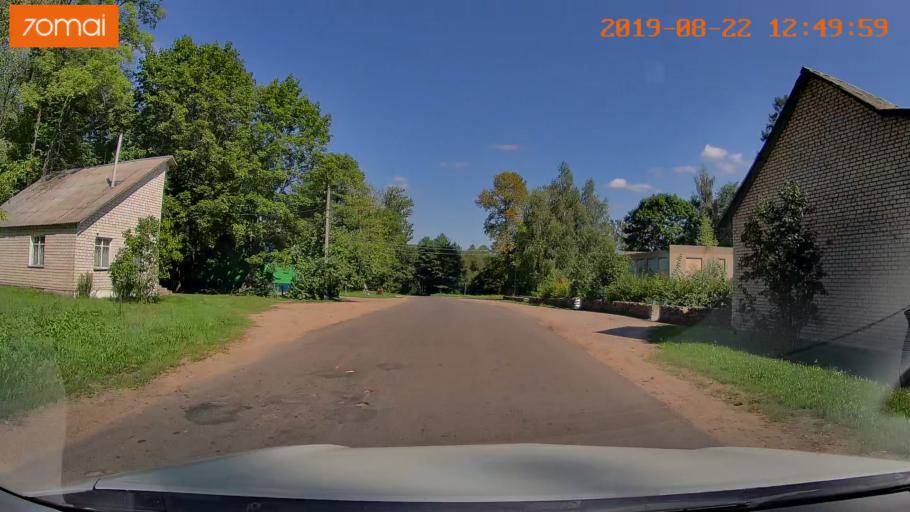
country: BY
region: Minsk
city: Prawdzinski
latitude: 53.4577
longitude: 27.6399
